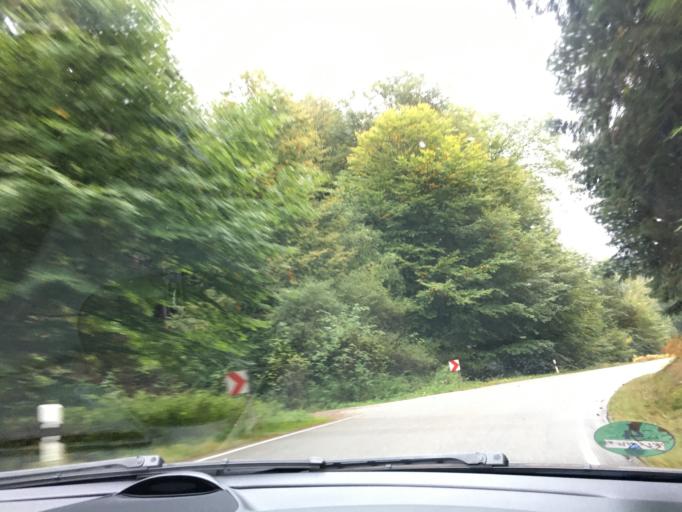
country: DE
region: Rheinland-Pfalz
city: Schmalenberg
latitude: 49.3439
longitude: 7.7326
